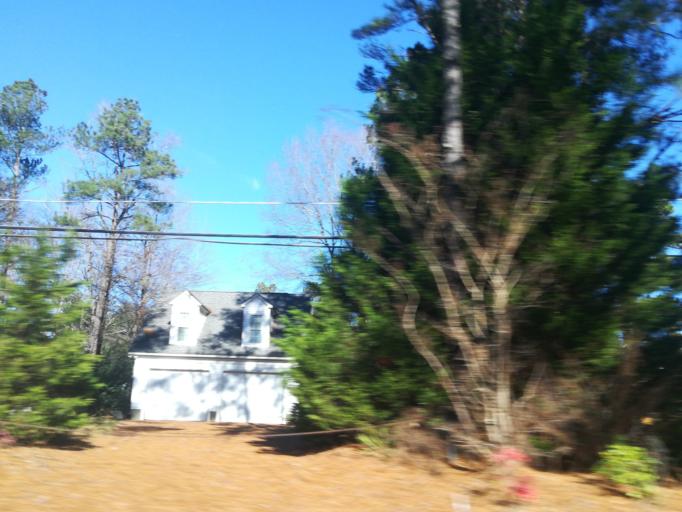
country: US
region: North Carolina
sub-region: Durham County
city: Durham
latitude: 36.0327
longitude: -78.9826
